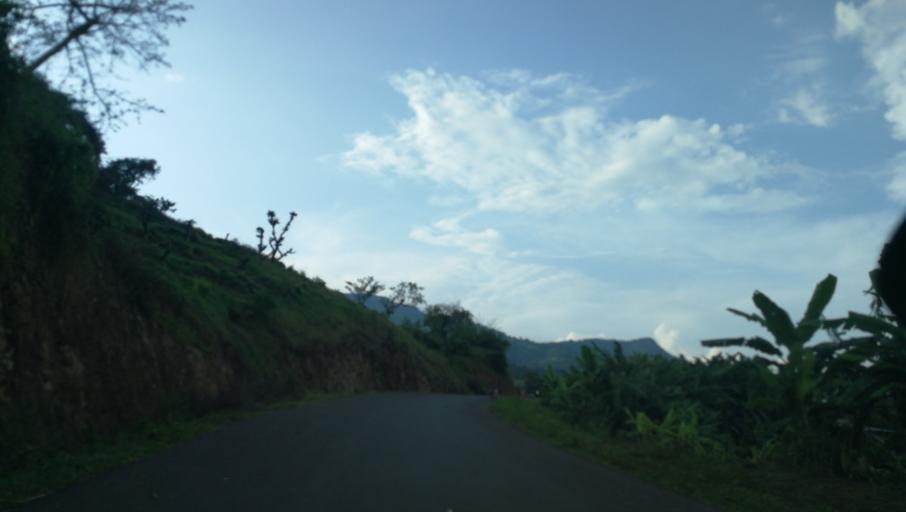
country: ET
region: Southern Nations, Nationalities, and People's Region
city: Areka
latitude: 6.8605
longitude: 37.2623
